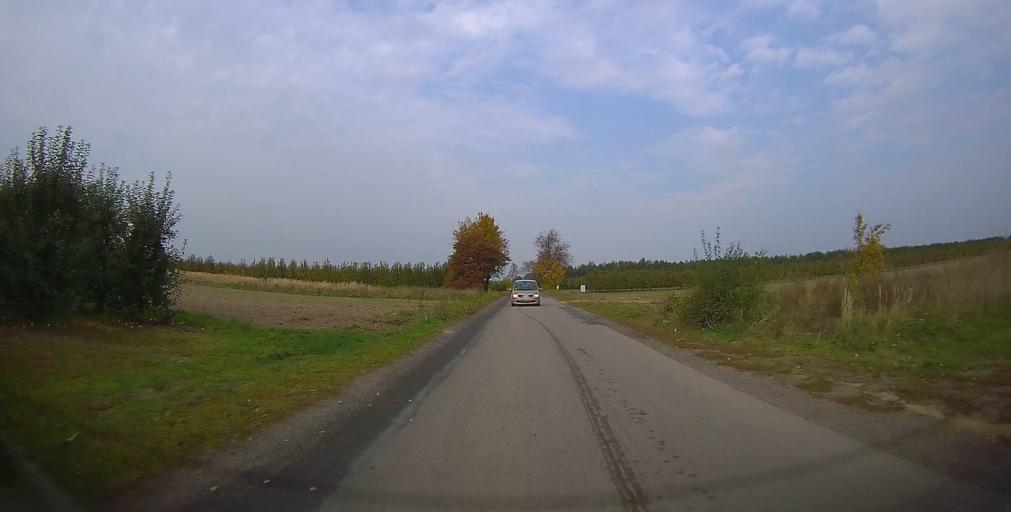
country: PL
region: Masovian Voivodeship
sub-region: Powiat grojecki
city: Mogielnica
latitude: 51.6521
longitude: 20.7248
